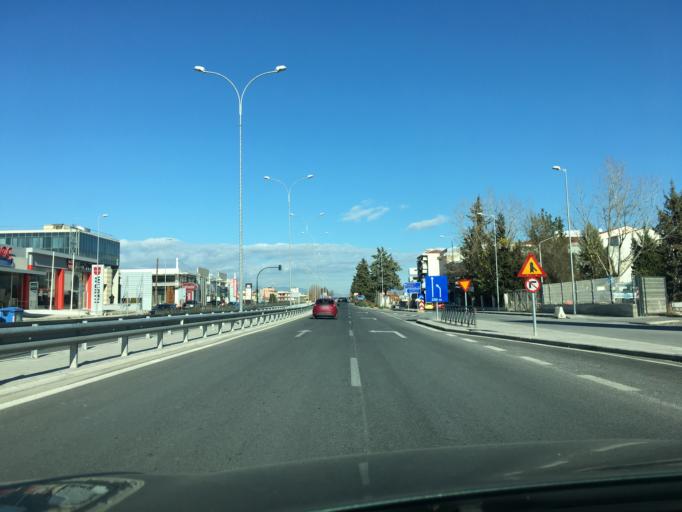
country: GR
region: Thessaly
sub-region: Nomos Larisis
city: Larisa
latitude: 39.6278
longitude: 22.4326
